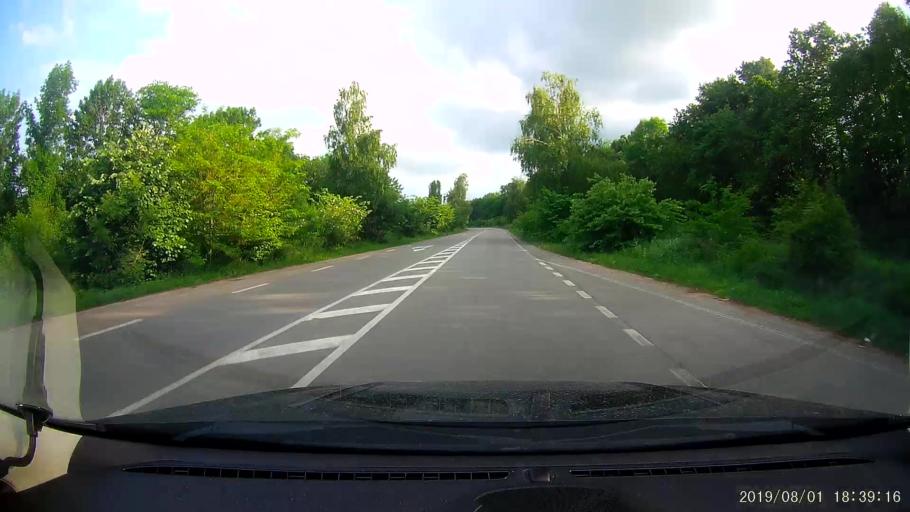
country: BG
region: Shumen
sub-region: Obshtina Khitrino
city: Gara Khitrino
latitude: 43.3889
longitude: 26.9170
